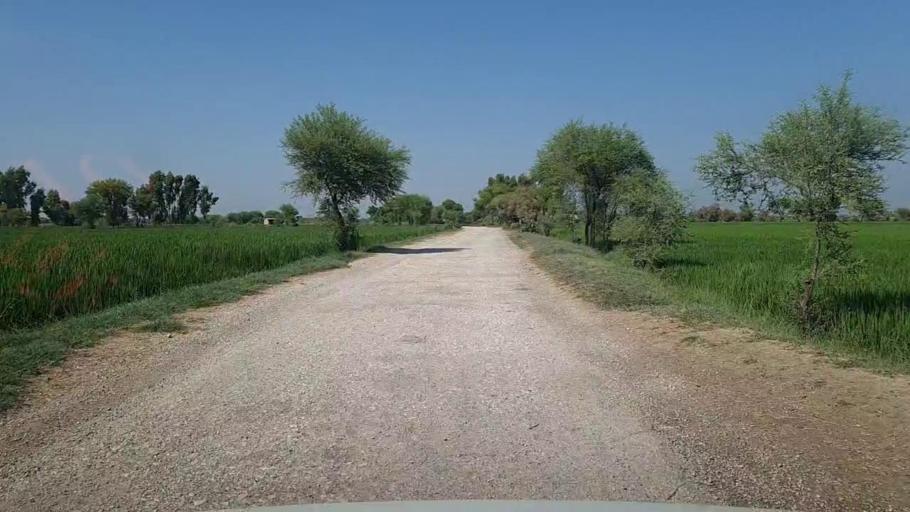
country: PK
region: Sindh
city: Kandhkot
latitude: 28.3305
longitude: 69.3672
